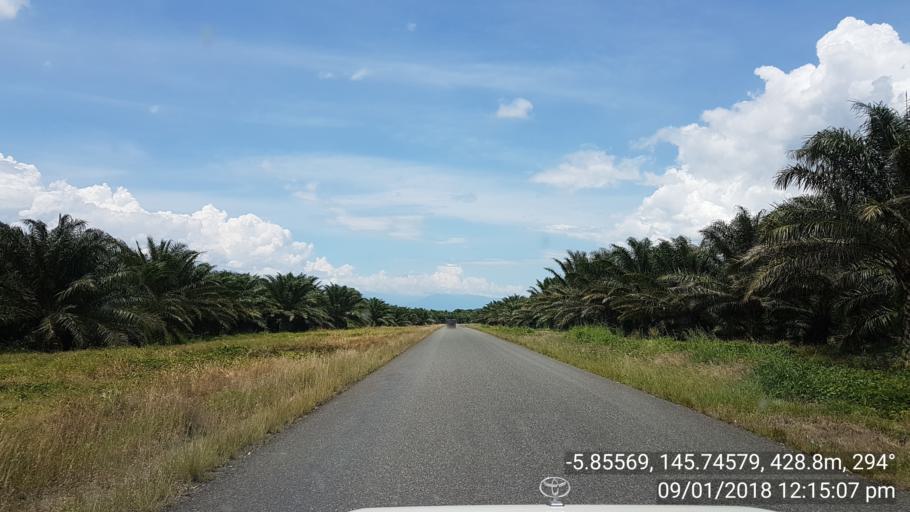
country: PG
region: Eastern Highlands
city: Goroka
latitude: -5.8556
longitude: 145.7458
